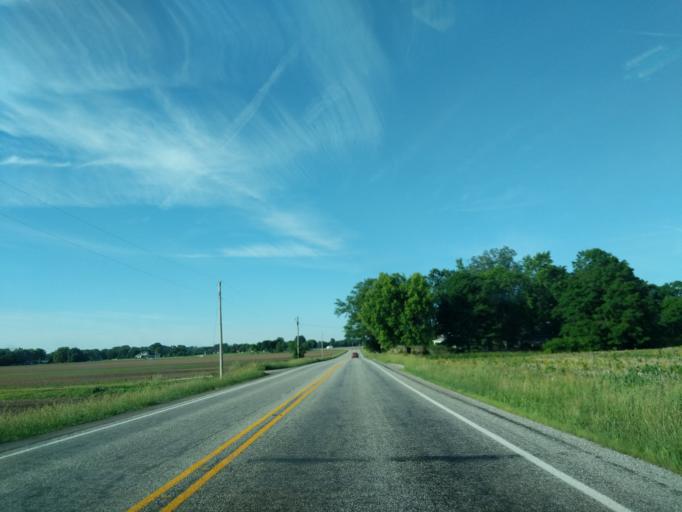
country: US
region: Indiana
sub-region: Madison County
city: Pendleton
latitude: 39.9726
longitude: -85.7564
